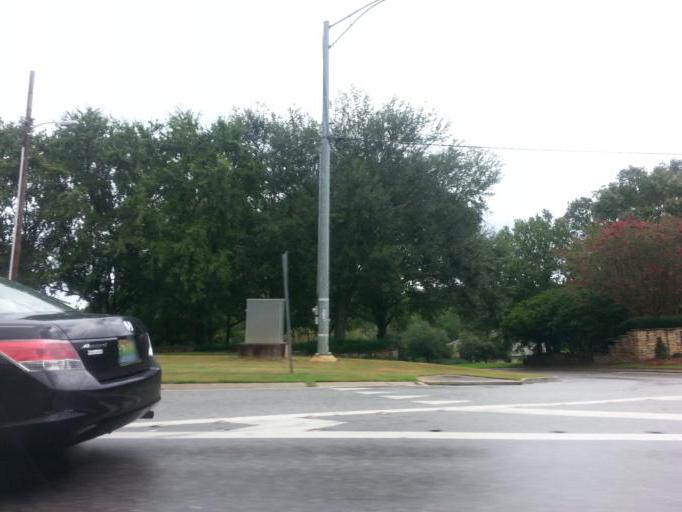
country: US
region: Alabama
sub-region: Baldwin County
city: Daphne
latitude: 30.5678
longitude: -87.8944
